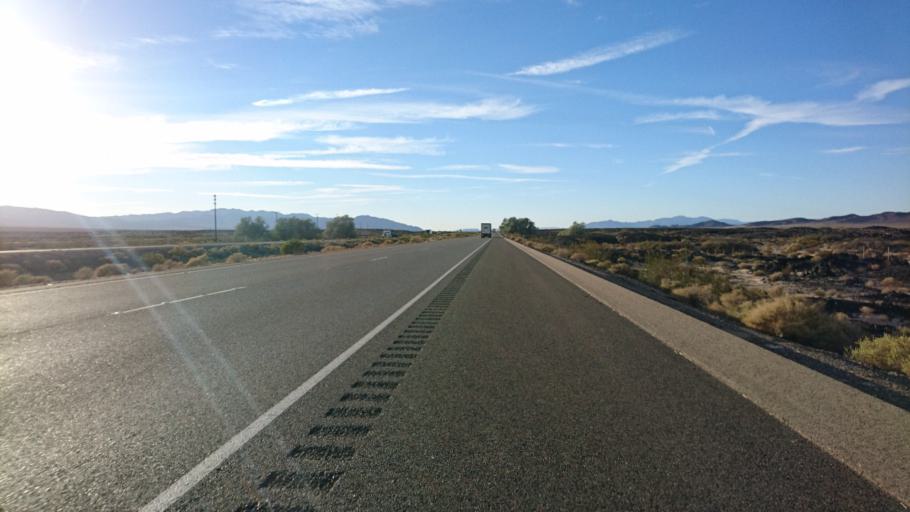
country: US
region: California
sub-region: San Bernardino County
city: Fort Irwin
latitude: 34.7941
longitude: -116.4934
